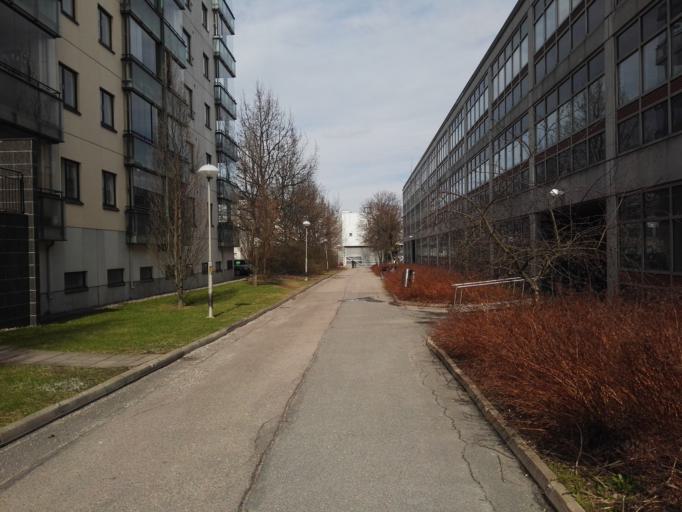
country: FI
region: Paijanne Tavastia
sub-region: Lahti
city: Lahti
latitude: 60.9844
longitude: 25.6637
